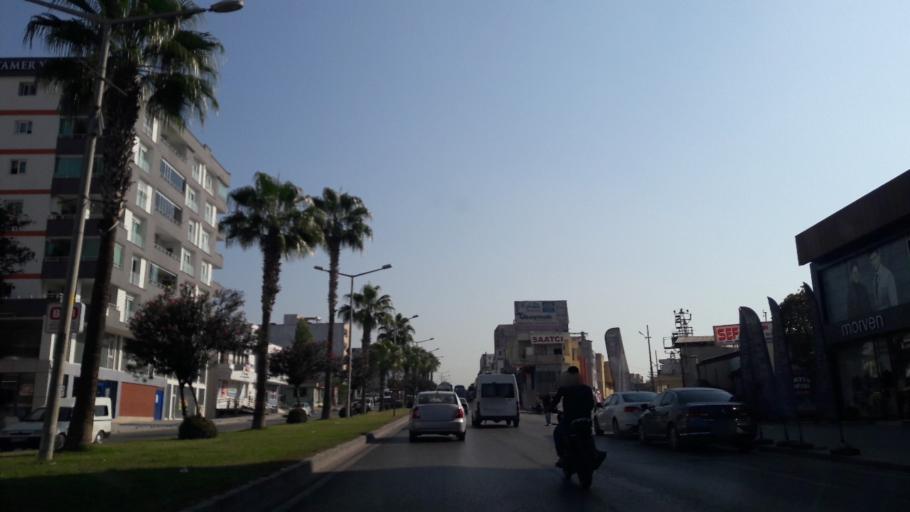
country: TR
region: Adana
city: Yuregir
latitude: 37.0306
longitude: 35.4073
